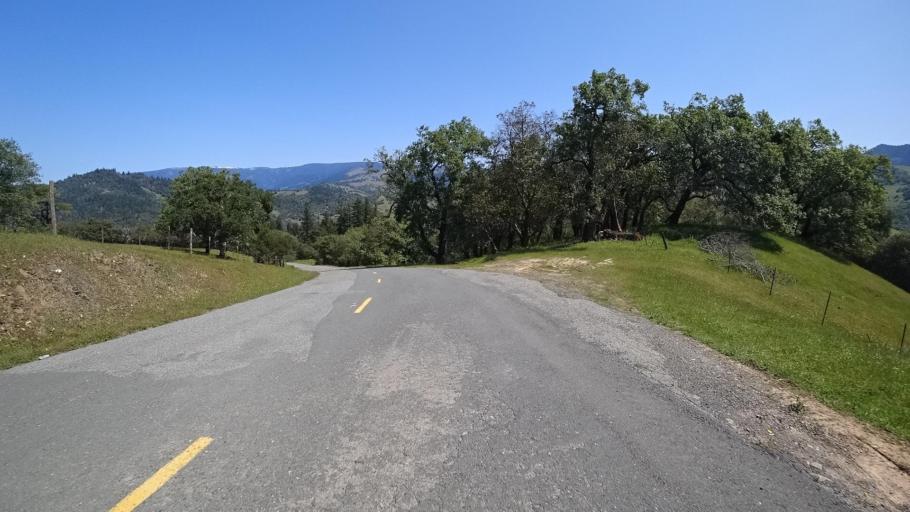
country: US
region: California
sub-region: Humboldt County
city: Redway
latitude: 40.1654
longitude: -123.6118
